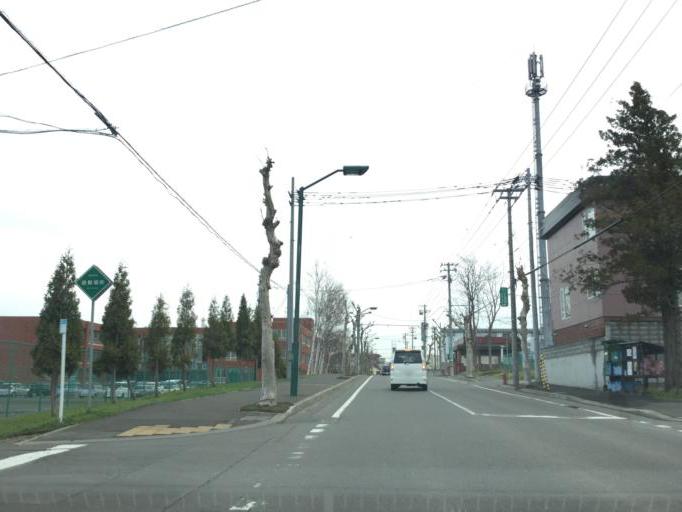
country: JP
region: Hokkaido
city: Iwamizawa
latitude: 43.2094
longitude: 141.7824
